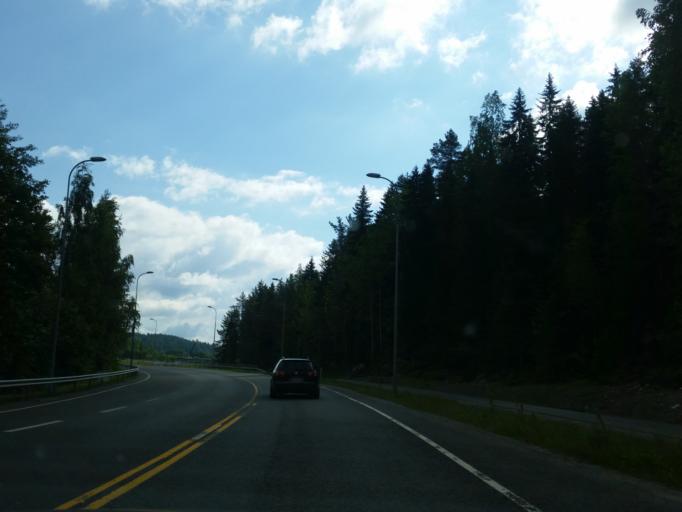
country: FI
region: Northern Savo
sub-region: Kuopio
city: Kuopio
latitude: 62.8397
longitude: 27.5928
